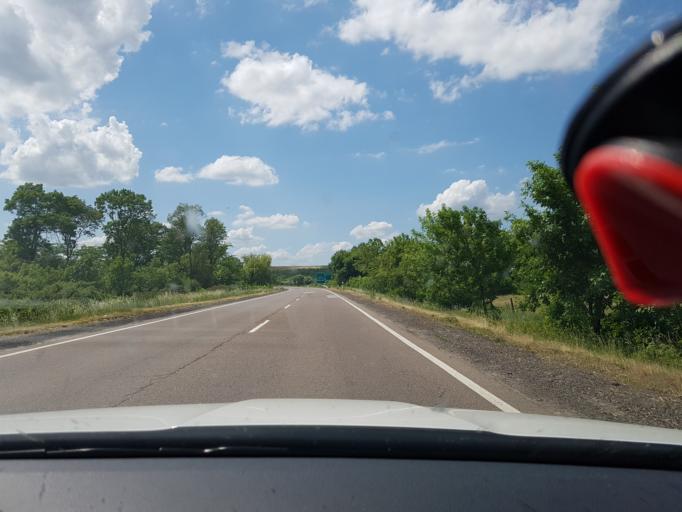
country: HU
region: Heves
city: Karacsond
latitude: 47.7413
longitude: 20.0942
